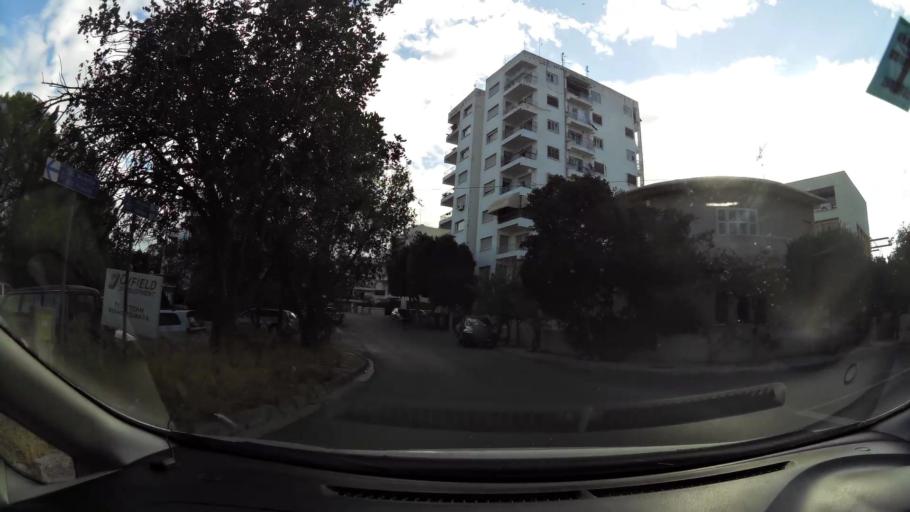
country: CY
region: Lefkosia
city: Nicosia
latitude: 35.1476
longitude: 33.3575
